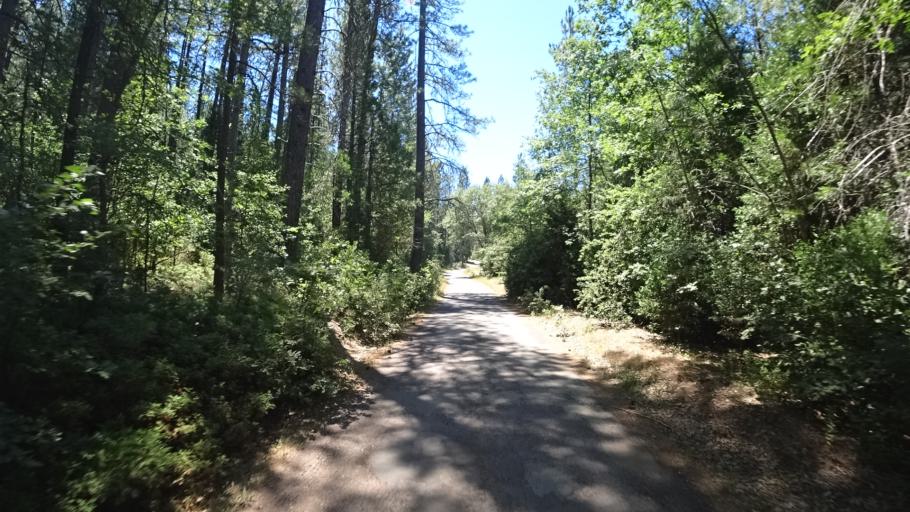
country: US
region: California
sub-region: Calaveras County
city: Arnold
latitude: 38.2586
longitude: -120.4169
